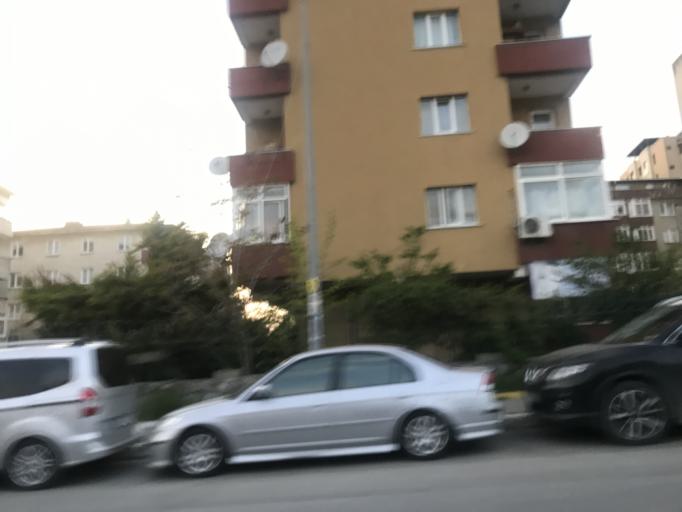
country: TR
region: Istanbul
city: Umraniye
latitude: 41.0336
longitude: 29.0974
